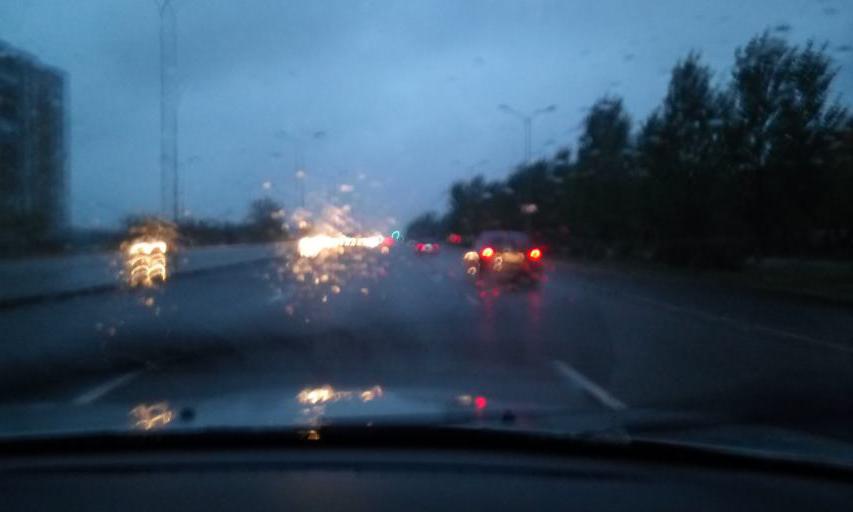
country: KZ
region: Astana Qalasy
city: Astana
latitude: 51.1904
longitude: 71.3374
